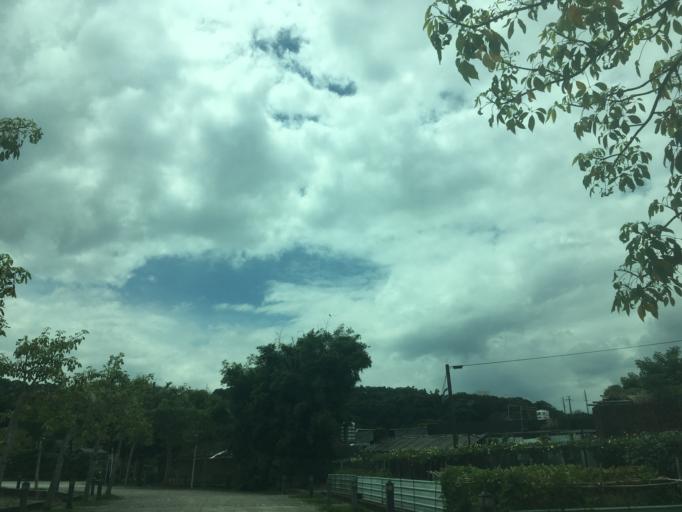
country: TW
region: Taiwan
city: Daxi
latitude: 24.8914
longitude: 121.2952
